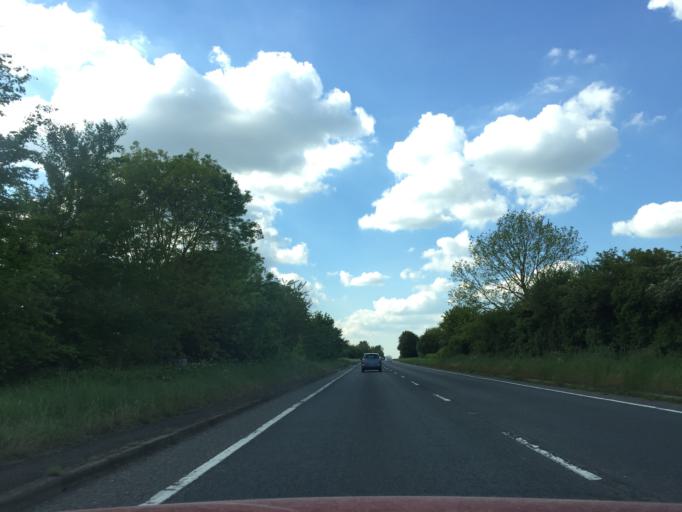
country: GB
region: England
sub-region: Milton Keynes
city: Castlethorpe
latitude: 52.0878
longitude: -0.8706
